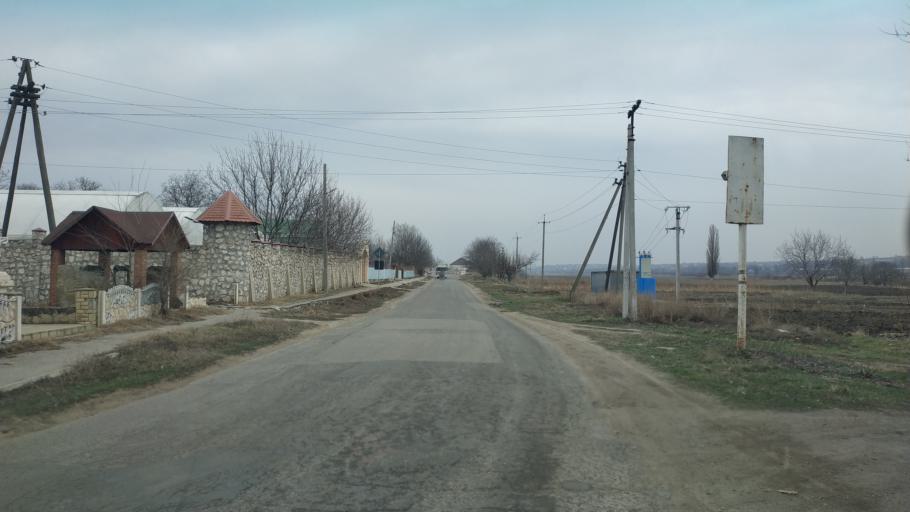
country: MD
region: Chisinau
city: Singera
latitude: 46.9329
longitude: 28.9816
